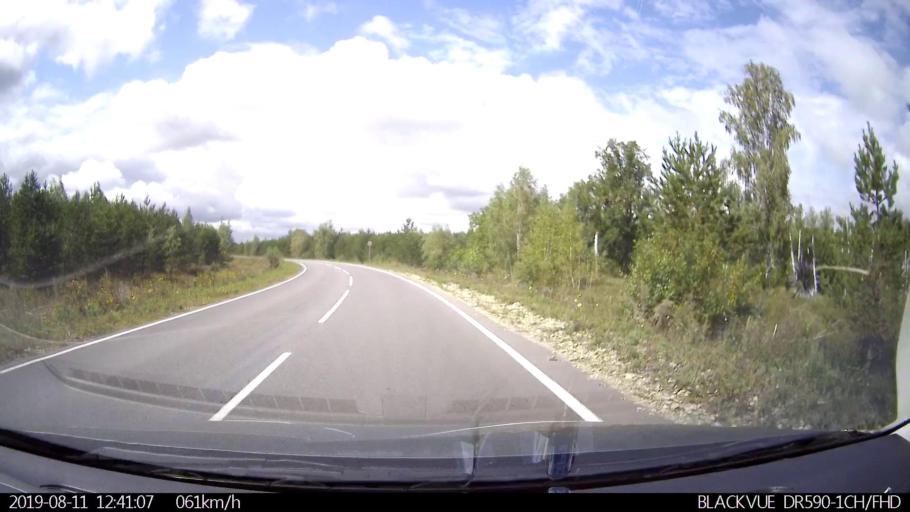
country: RU
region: Ulyanovsk
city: Ignatovka
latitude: 53.8423
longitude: 47.7712
